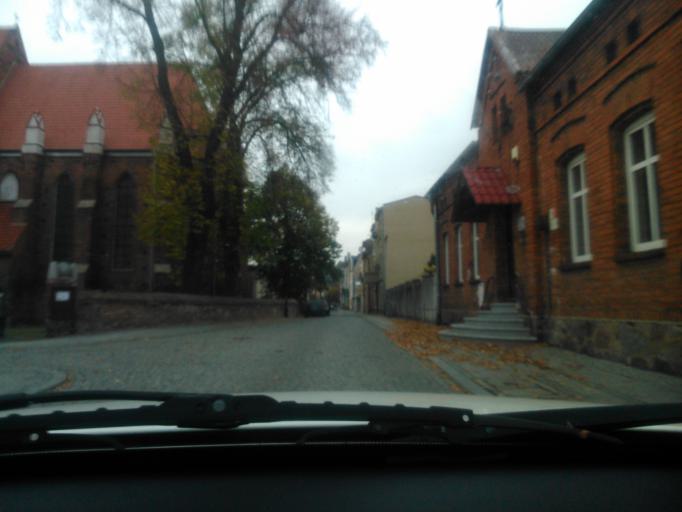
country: PL
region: Kujawsko-Pomorskie
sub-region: Powiat golubsko-dobrzynski
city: Golub-Dobrzyn
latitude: 53.1129
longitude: 19.0562
